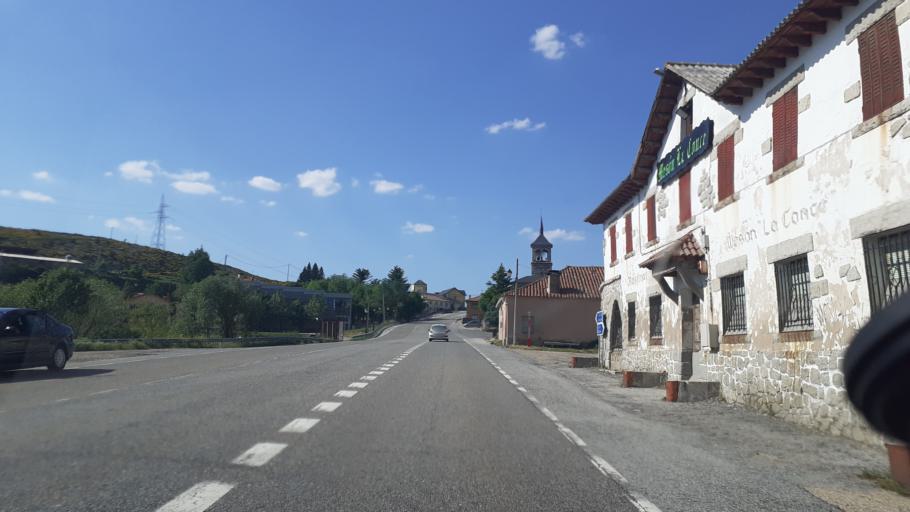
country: ES
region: Madrid
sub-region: Provincia de Madrid
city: Somosierra
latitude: 41.1312
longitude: -3.5809
